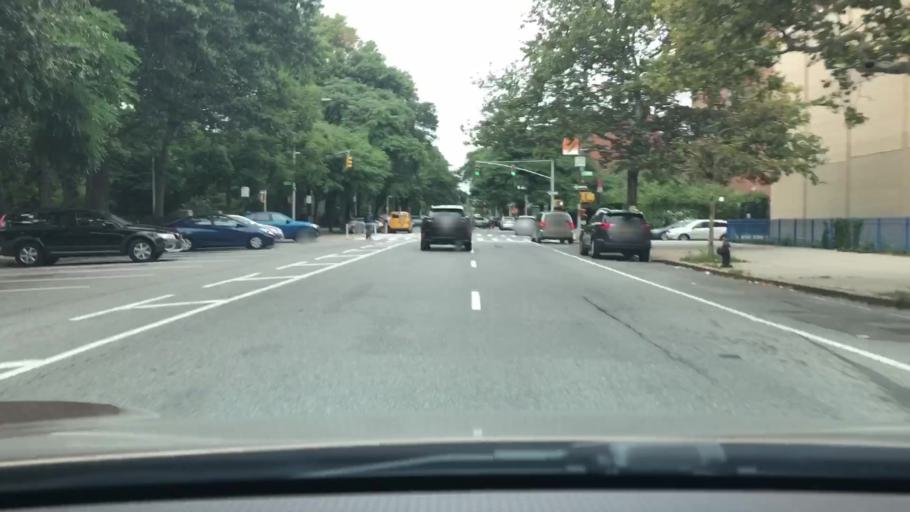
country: US
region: New York
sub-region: New York County
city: Manhattan
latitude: 40.8028
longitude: -73.9429
